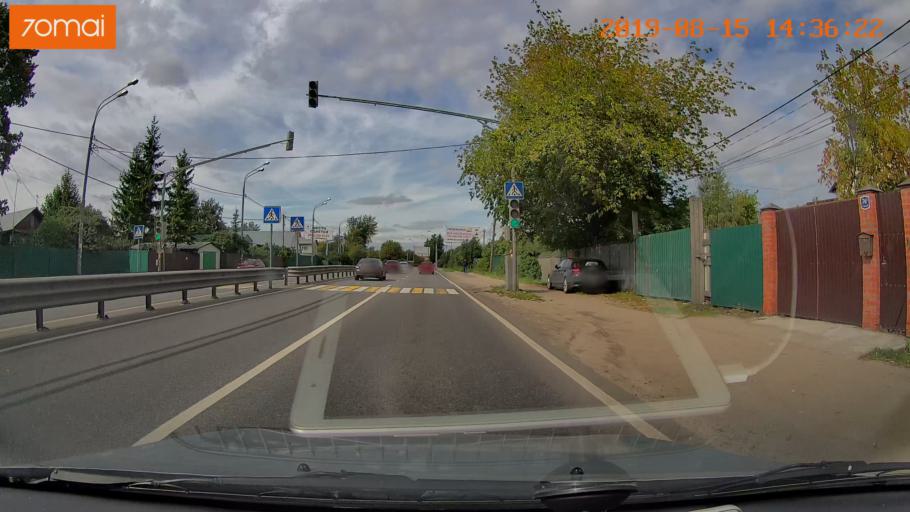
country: RU
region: Moskovskaya
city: Tomilino
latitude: 55.6457
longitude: 37.9355
